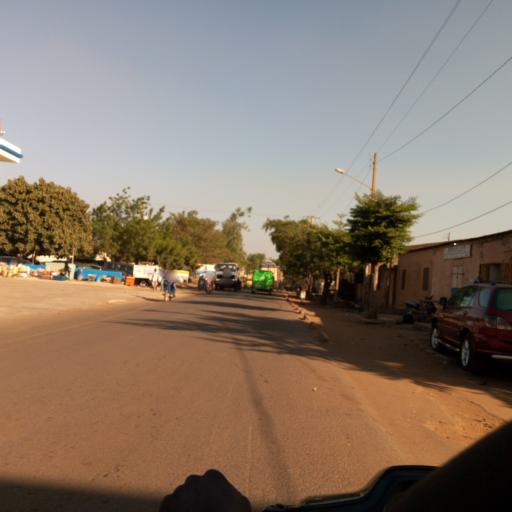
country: ML
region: Bamako
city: Bamako
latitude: 12.6550
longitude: -8.0234
